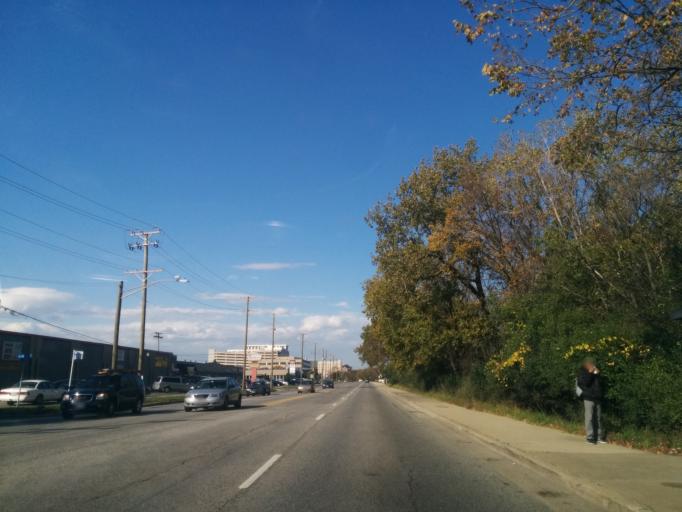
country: US
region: Illinois
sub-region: Cook County
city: Schiller Park
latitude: 41.9679
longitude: -87.8616
